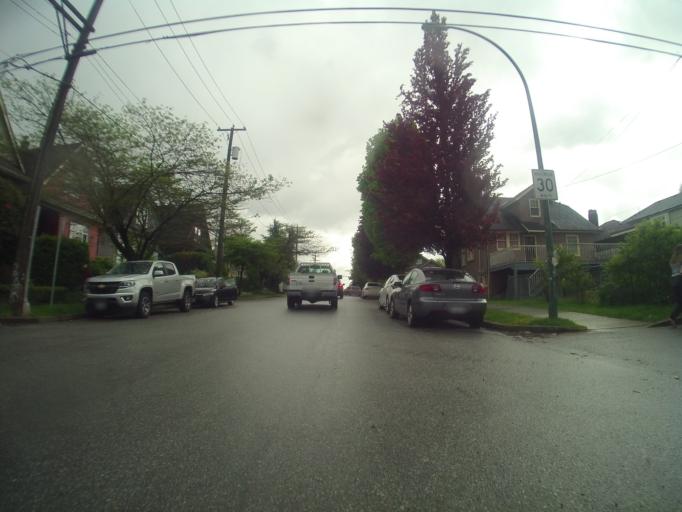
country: CA
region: British Columbia
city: Vancouver
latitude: 49.2638
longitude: -123.0737
